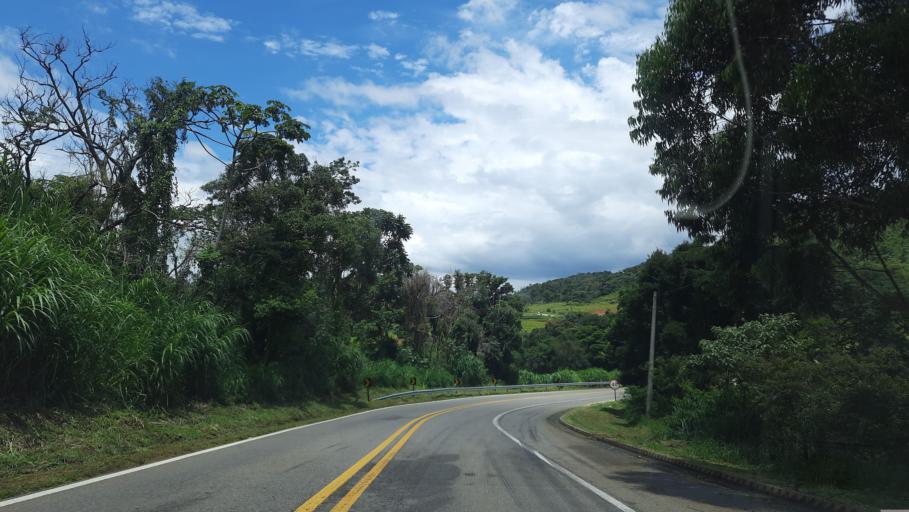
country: BR
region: Sao Paulo
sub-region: Vargem Grande Do Sul
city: Vargem Grande do Sul
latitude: -21.8266
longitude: -46.7755
